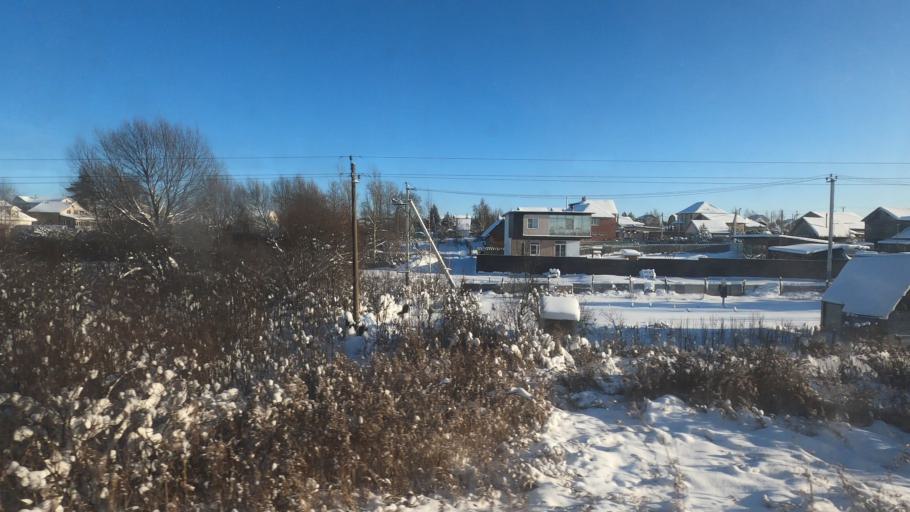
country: RU
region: Moskovskaya
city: Orud'yevo
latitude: 56.4158
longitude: 37.4970
